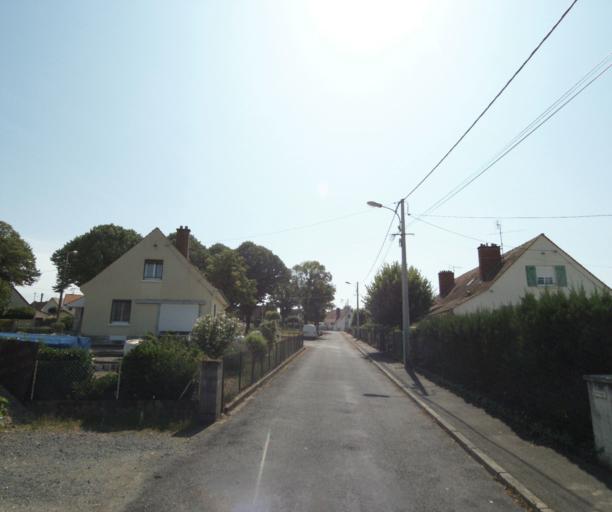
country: FR
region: Bourgogne
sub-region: Departement de Saone-et-Loire
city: Gueugnon
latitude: 46.5997
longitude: 4.0714
